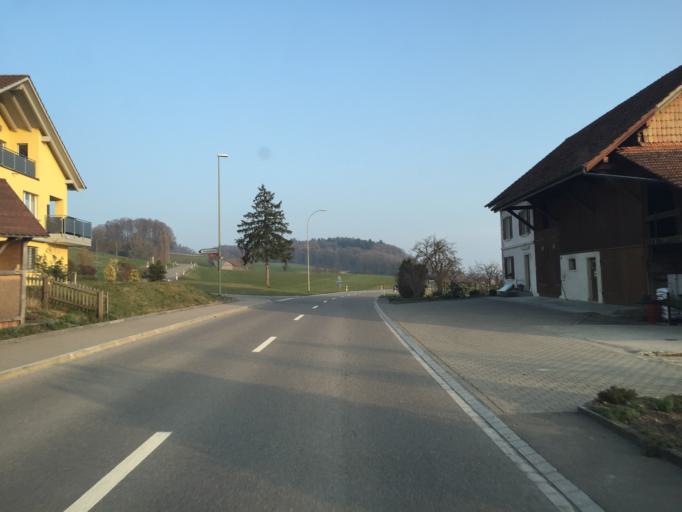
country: CH
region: Zurich
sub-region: Bezirk Andelfingen
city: Marthalen
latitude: 47.6513
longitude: 8.6581
